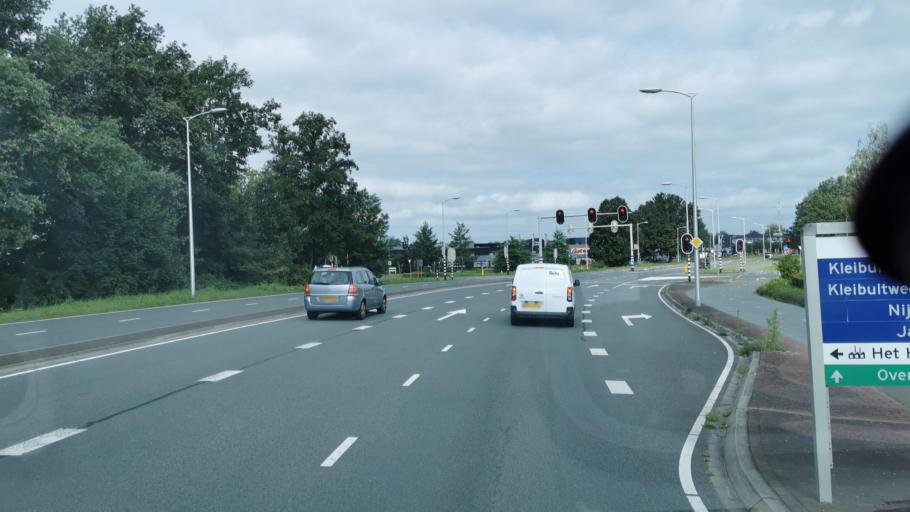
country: NL
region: Overijssel
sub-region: Gemeente Oldenzaal
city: Oldenzaal
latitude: 52.2932
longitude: 6.9250
